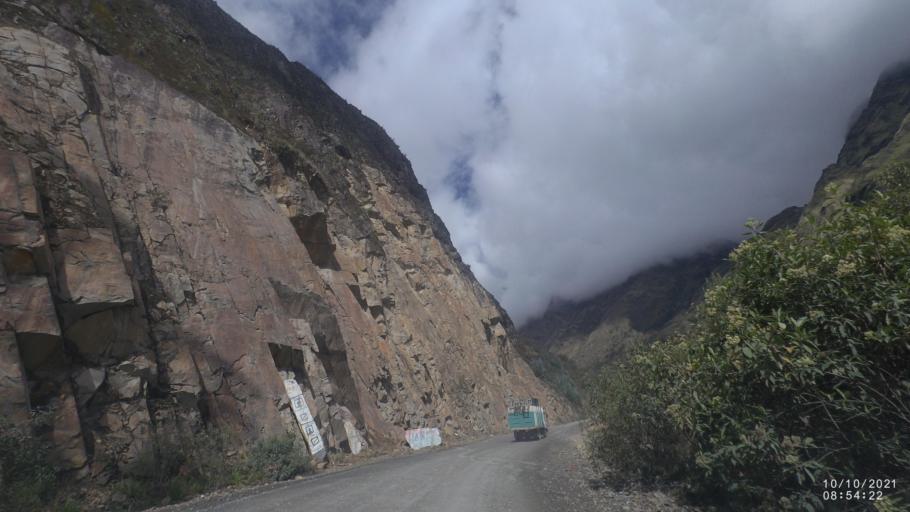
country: BO
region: La Paz
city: Quime
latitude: -16.9888
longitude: -67.2342
